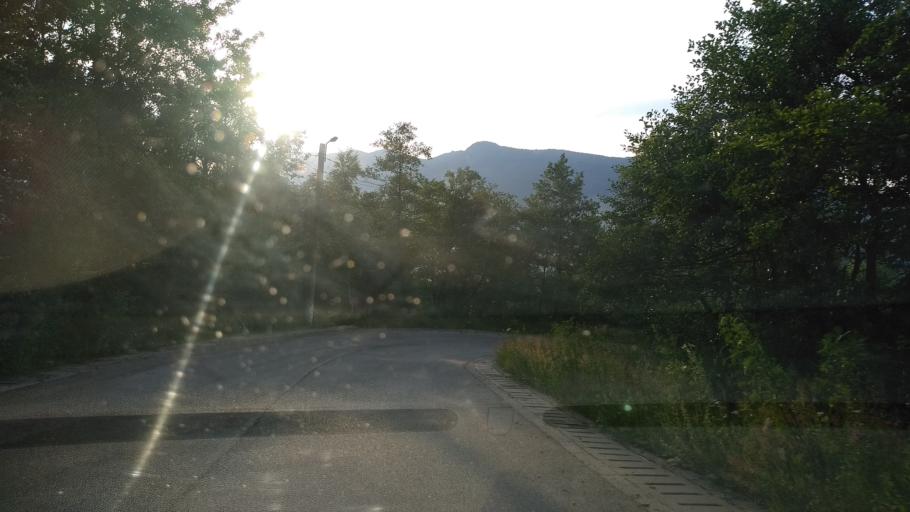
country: RO
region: Hunedoara
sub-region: Municipiul  Vulcan
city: Jiu-Paroseni
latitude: 45.3634
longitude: 23.2850
